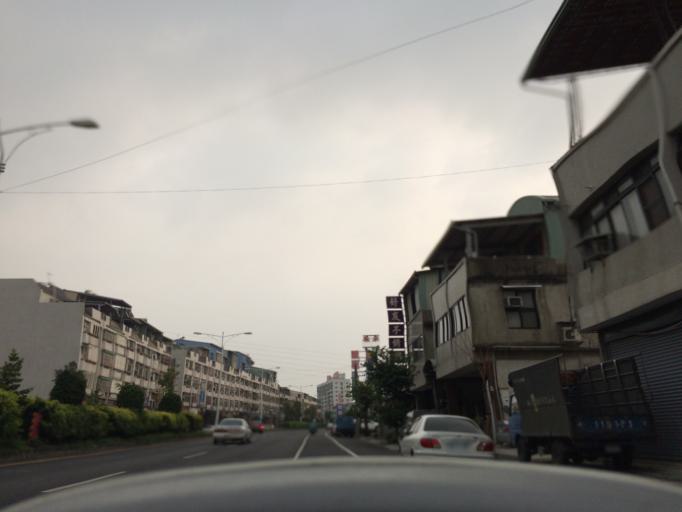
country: TW
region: Taiwan
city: Zhongxing New Village
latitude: 24.0492
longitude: 120.6938
